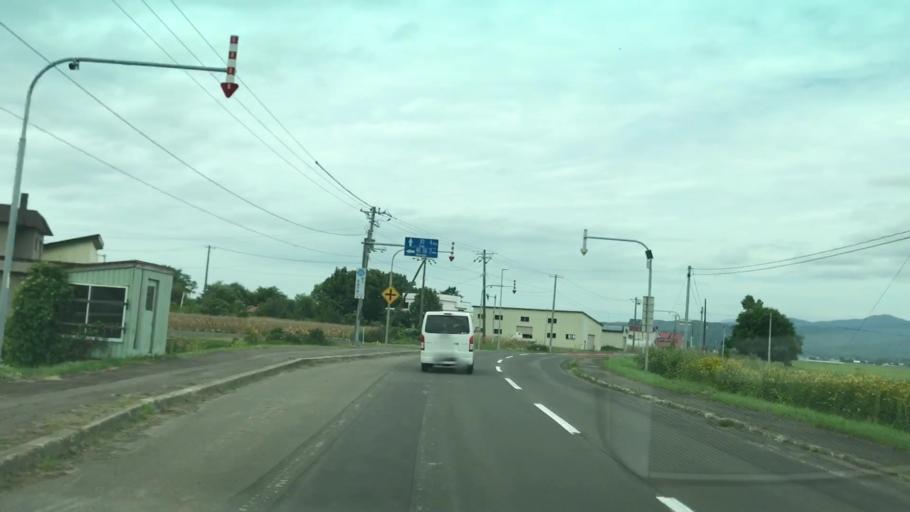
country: JP
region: Hokkaido
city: Iwanai
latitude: 43.0019
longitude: 140.5865
